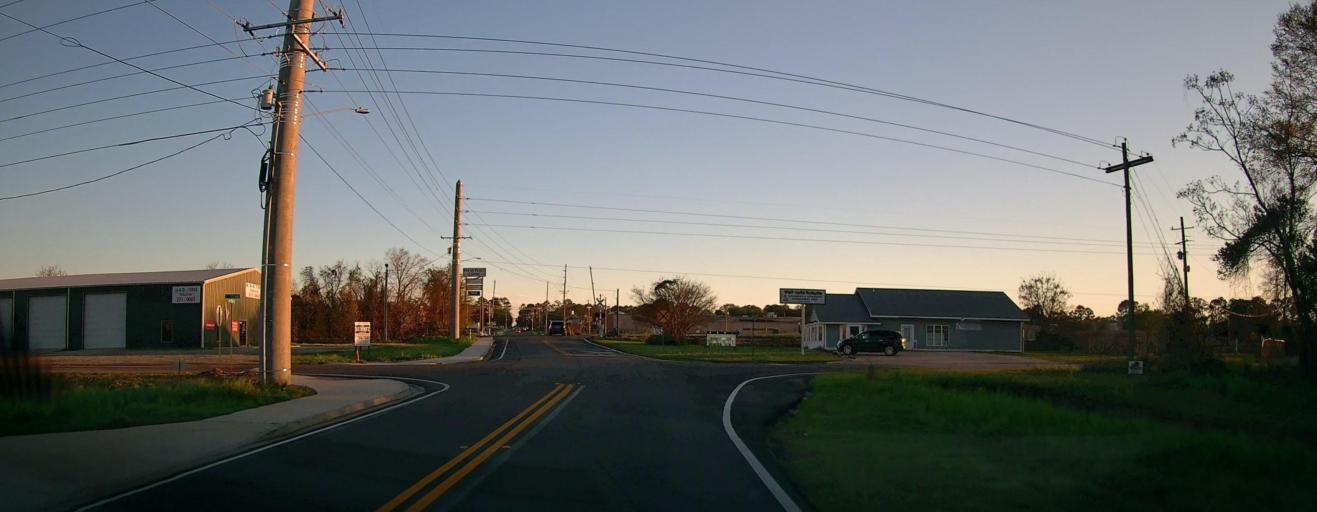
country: US
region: Georgia
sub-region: Crisp County
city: Cordele
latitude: 31.9674
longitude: -83.7651
